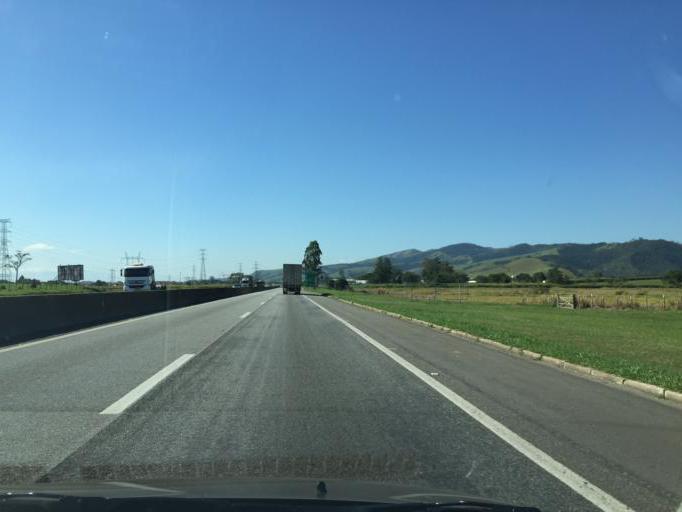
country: BR
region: Sao Paulo
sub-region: Aparecida
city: Aparecida
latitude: -22.9116
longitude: -45.3238
